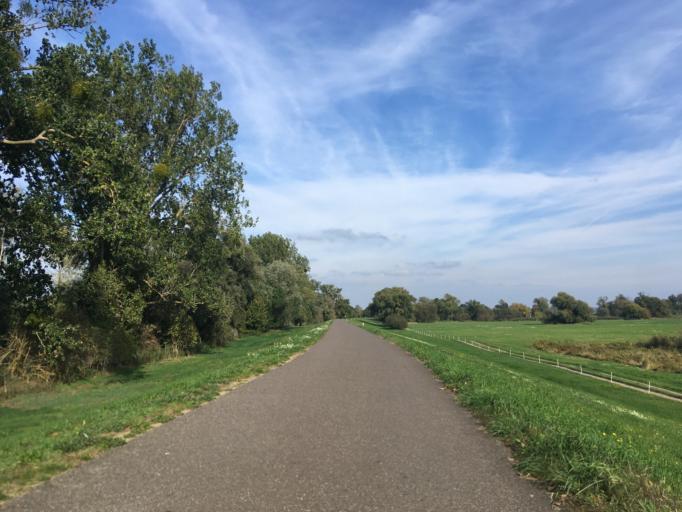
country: DE
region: Brandenburg
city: Schwedt (Oder)
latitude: 53.0485
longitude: 14.2822
